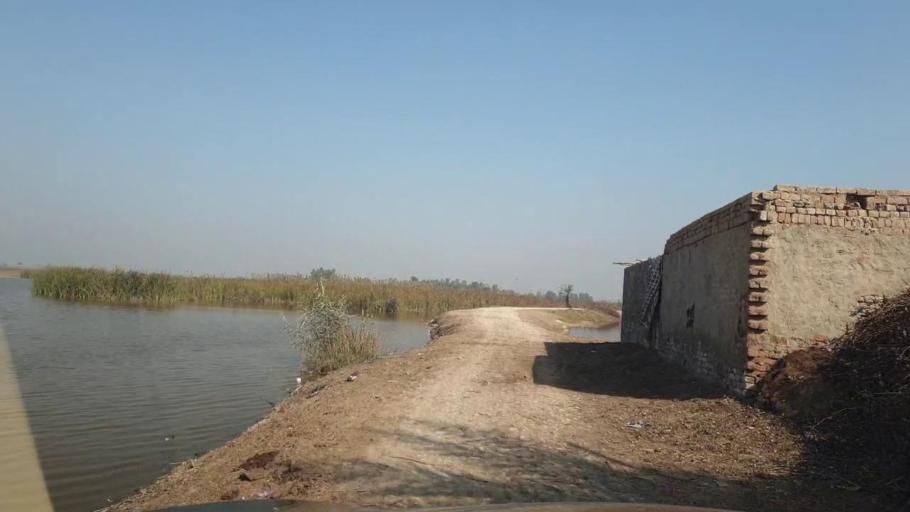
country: PK
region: Sindh
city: Ubauro
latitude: 28.1426
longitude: 69.7511
